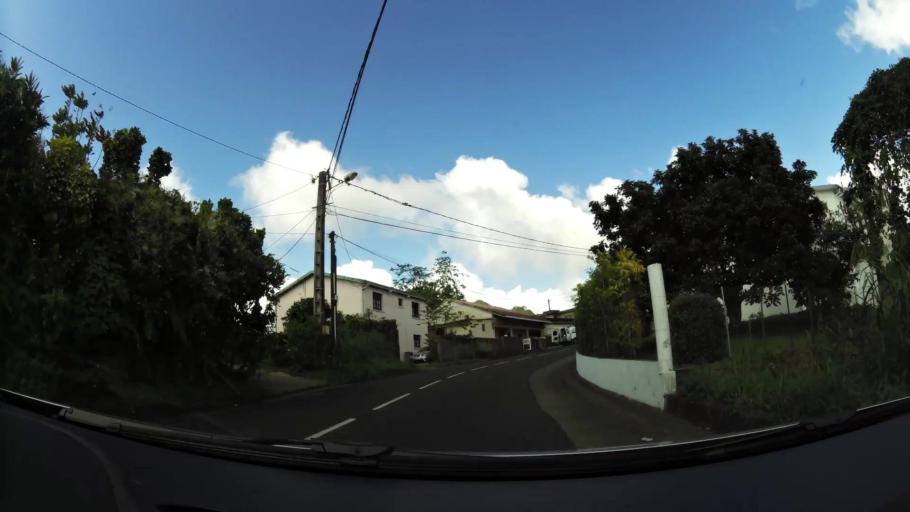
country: MQ
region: Martinique
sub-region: Martinique
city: Fort-de-France
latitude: 14.6559
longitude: -61.0857
